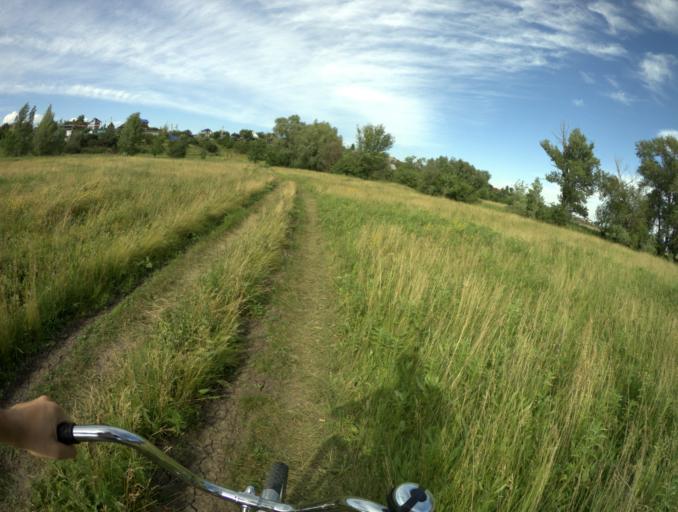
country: RU
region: Saratov
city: Yelshanka
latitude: 51.8031
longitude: 46.4621
